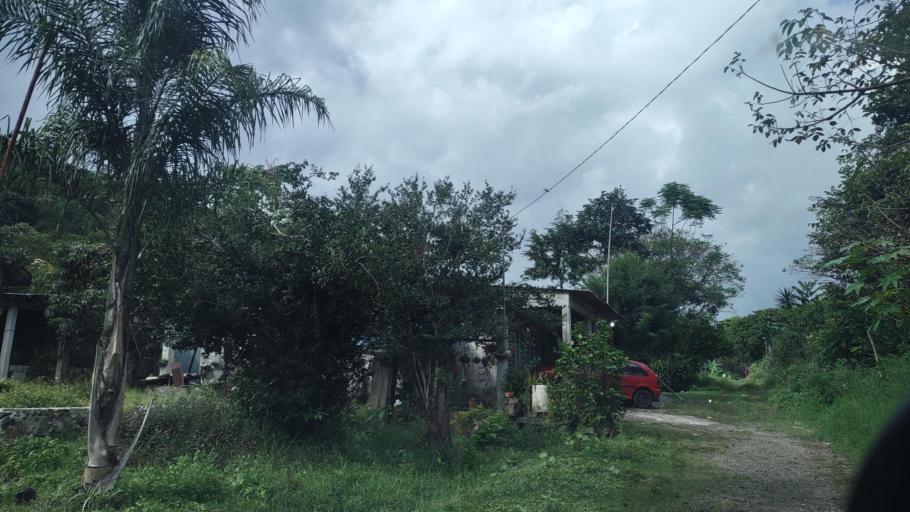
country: MX
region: Veracruz
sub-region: Fortin
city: Monte Salas
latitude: 18.9270
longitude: -97.0273
